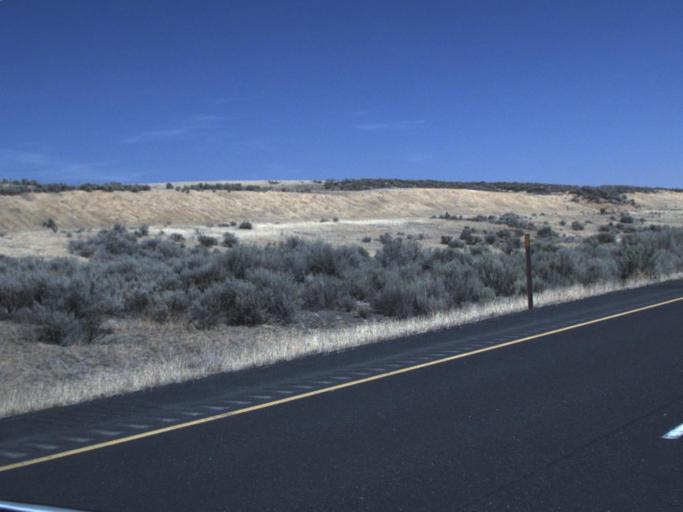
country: US
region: Washington
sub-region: Grant County
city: Warden
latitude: 47.0862
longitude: -118.9354
